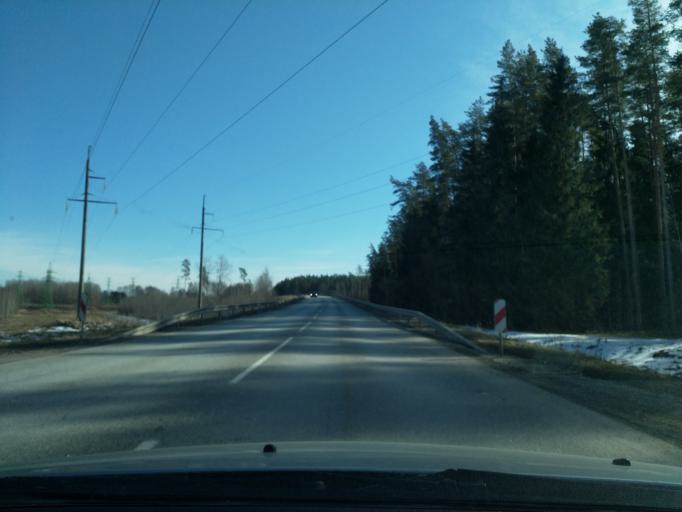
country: LV
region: Valmieras Rajons
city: Valmiera
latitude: 57.5110
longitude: 25.4293
